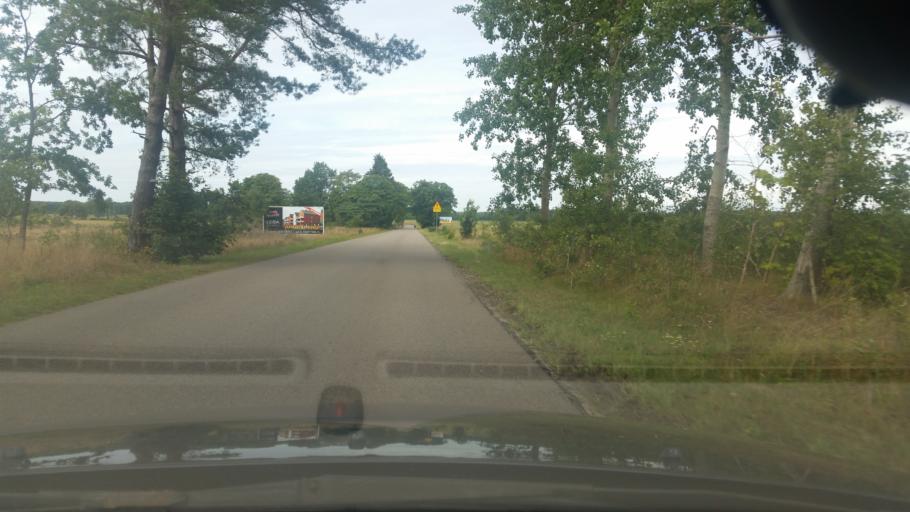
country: PL
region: Pomeranian Voivodeship
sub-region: Powiat leborski
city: Leba
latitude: 54.7282
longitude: 17.6109
